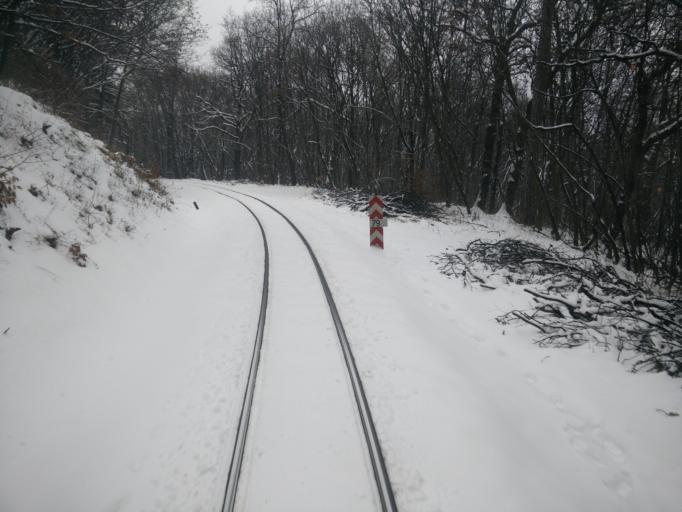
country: HU
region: Pest
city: Budakeszi
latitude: 47.5295
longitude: 18.9687
